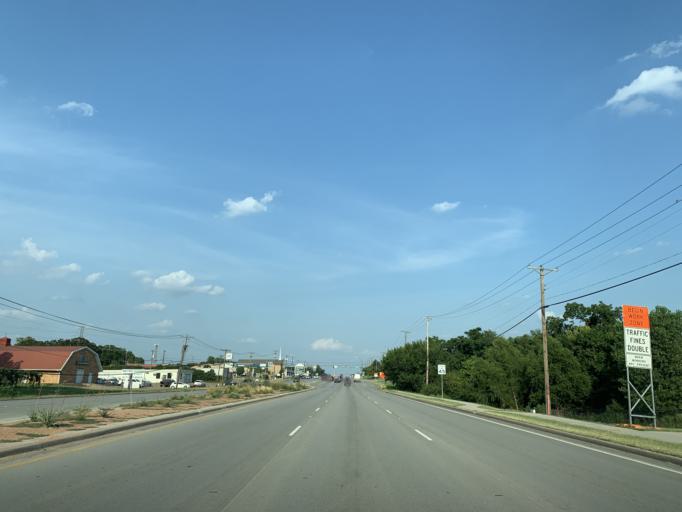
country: US
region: Texas
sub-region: Tarrant County
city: Hurst
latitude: 32.8091
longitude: -97.1894
